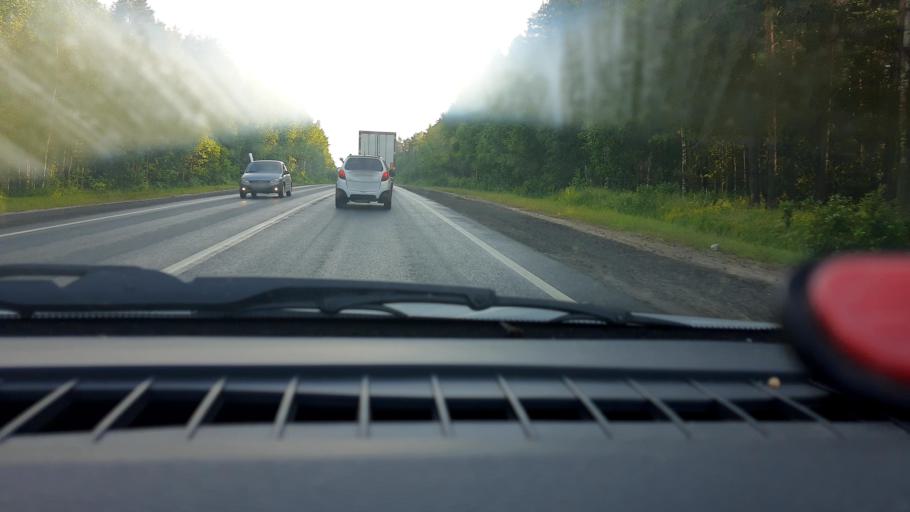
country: RU
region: Nizjnij Novgorod
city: Arzamas
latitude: 55.5090
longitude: 43.8970
